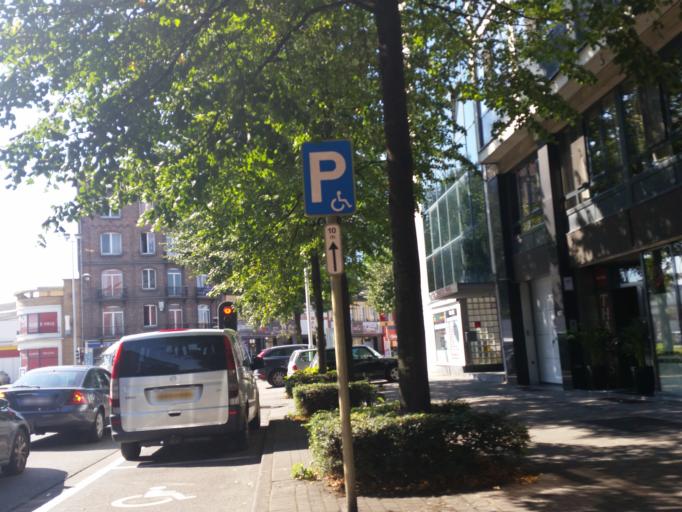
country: BE
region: Brussels Capital
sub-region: Bruxelles-Capitale
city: Brussels
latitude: 50.8332
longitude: 4.3310
